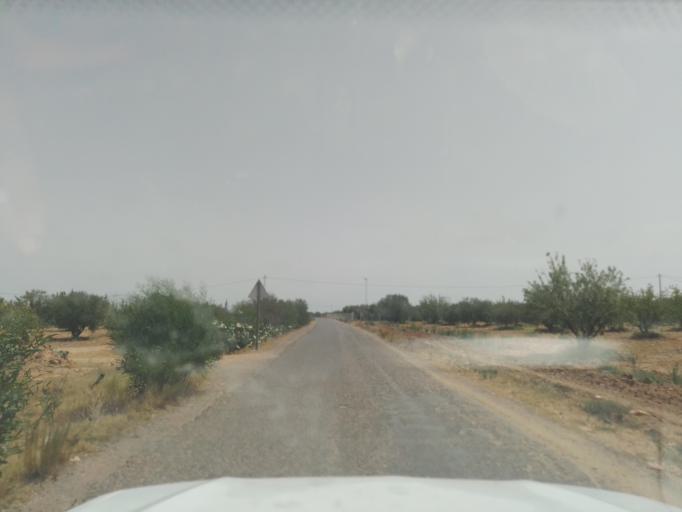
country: TN
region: Al Qasrayn
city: Kasserine
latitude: 35.2661
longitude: 9.0047
